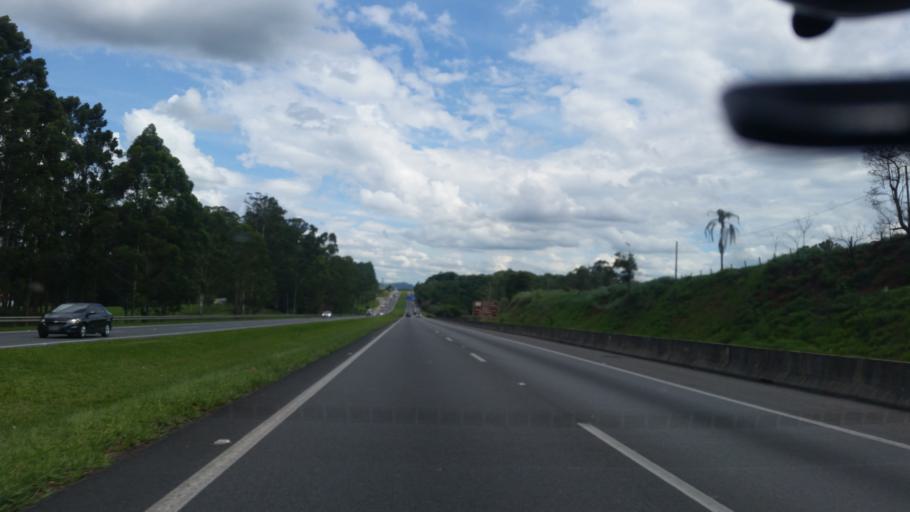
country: BR
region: Sao Paulo
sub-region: Itatiba
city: Itatiba
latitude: -22.9388
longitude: -46.8798
